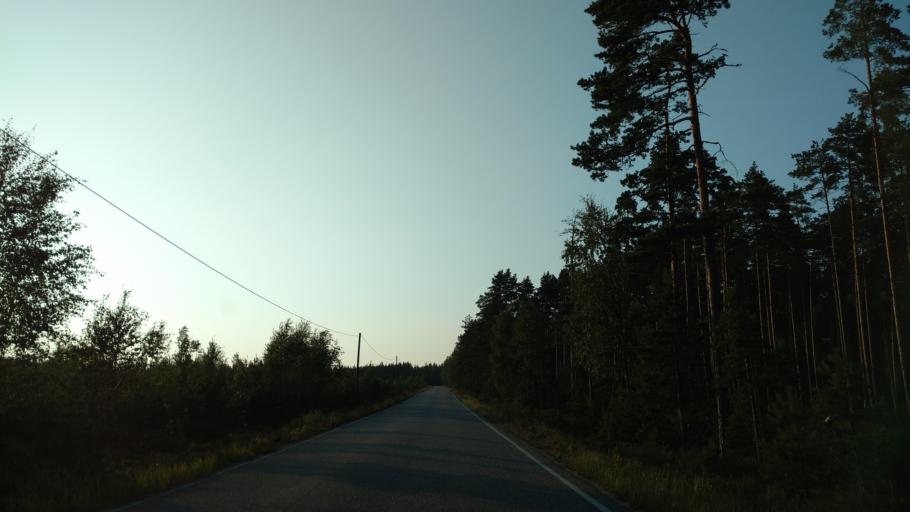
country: FI
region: Varsinais-Suomi
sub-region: Salo
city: Saerkisalo
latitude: 60.1937
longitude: 22.9455
